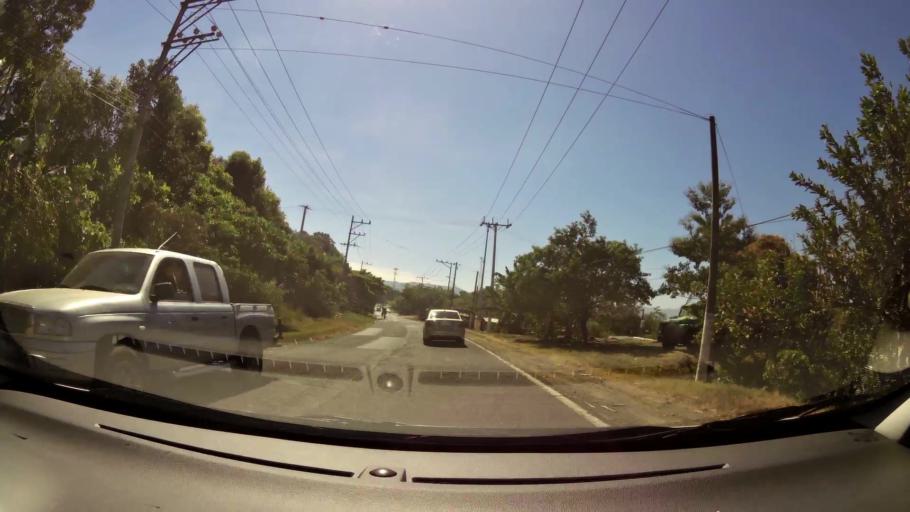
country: SV
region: La Libertad
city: San Juan Opico
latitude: 13.8158
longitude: -89.3567
